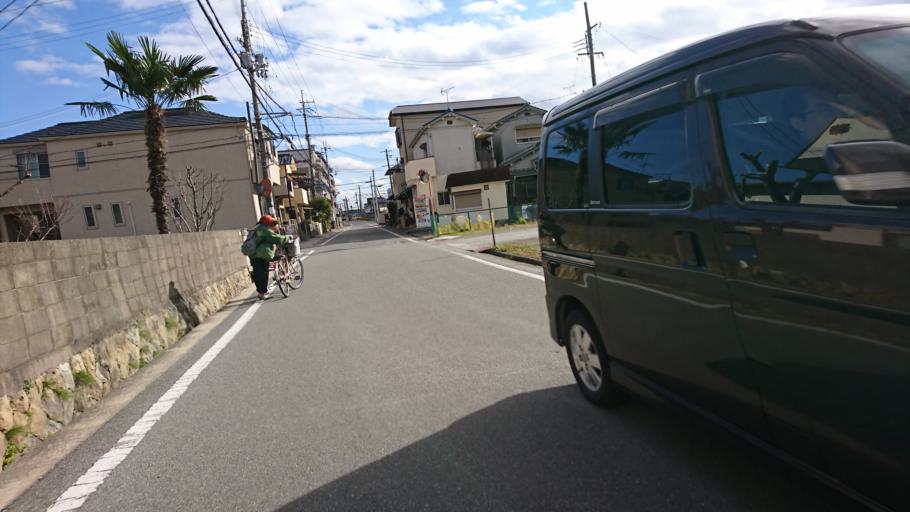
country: JP
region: Hyogo
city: Kakogawacho-honmachi
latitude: 34.7868
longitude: 134.8085
